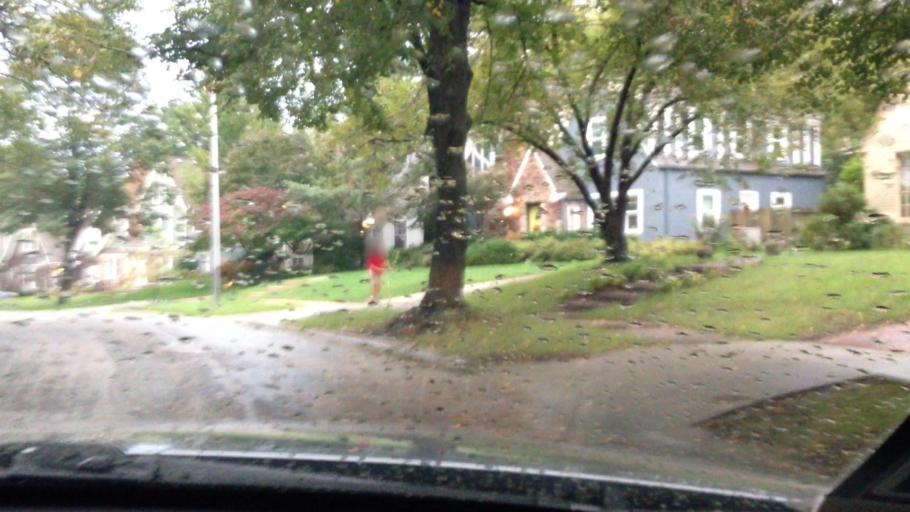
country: US
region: Kansas
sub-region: Johnson County
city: Mission Hills
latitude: 39.0016
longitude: -94.5986
